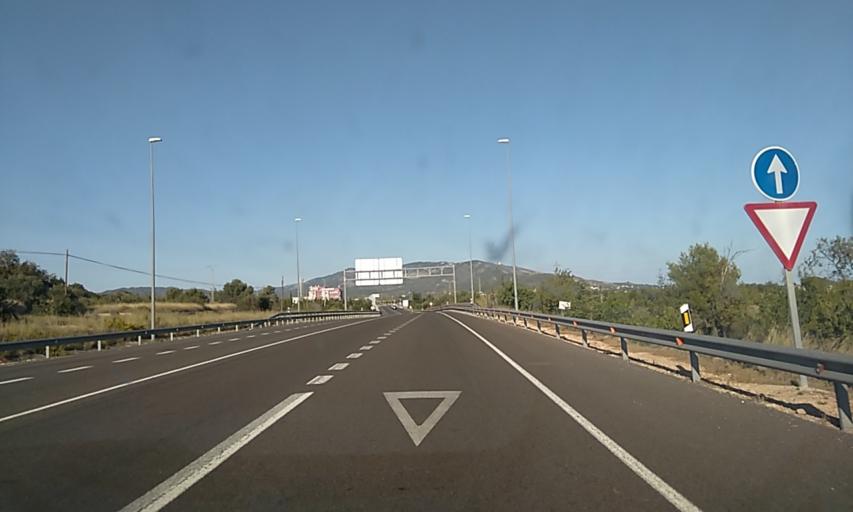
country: ES
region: Valencia
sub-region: Provincia de Castello
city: Torreblanca
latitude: 40.2298
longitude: 0.2164
